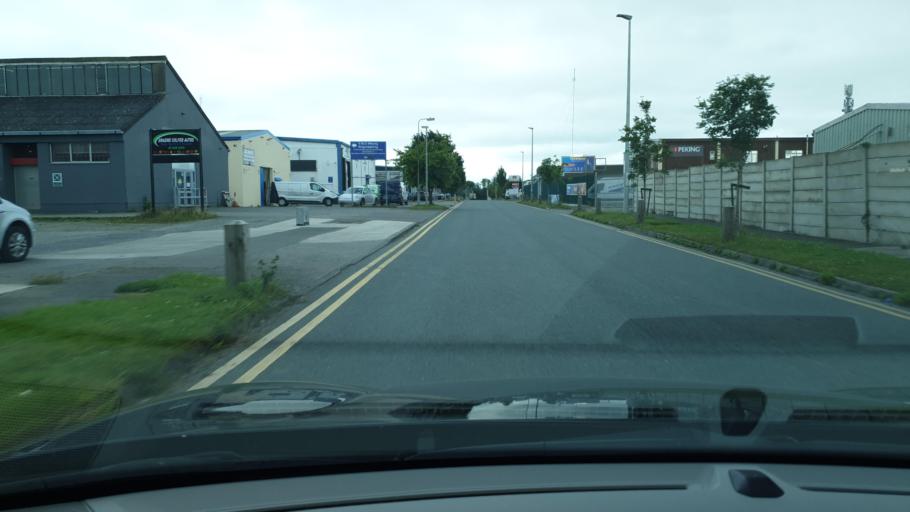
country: IE
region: Leinster
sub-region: An Mhi
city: Ashbourne
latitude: 53.5181
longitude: -6.4157
